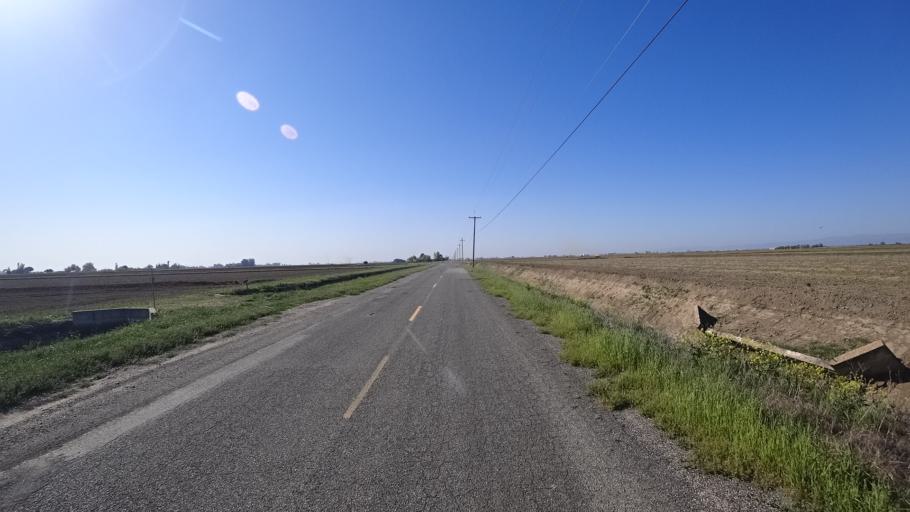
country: US
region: California
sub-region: Glenn County
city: Willows
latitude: 39.5693
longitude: -122.1171
